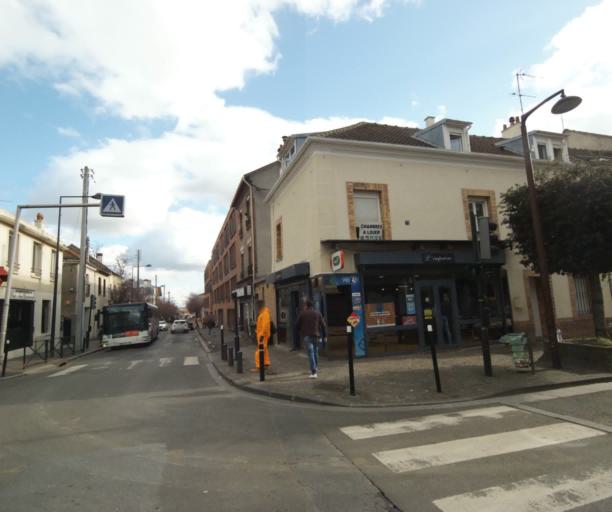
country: FR
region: Ile-de-France
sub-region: Departement de Seine-Saint-Denis
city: Pierrefitte-sur-Seine
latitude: 48.9677
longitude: 2.3620
